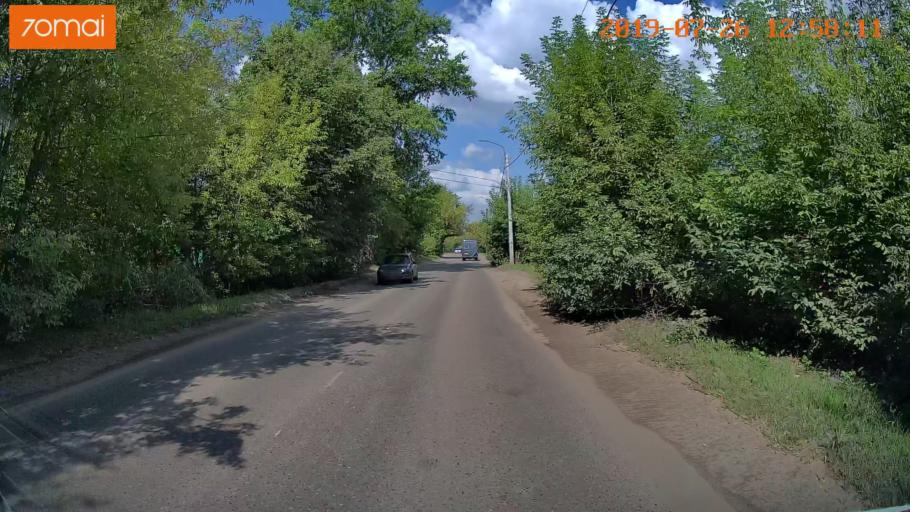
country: RU
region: Ivanovo
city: Bogorodskoye
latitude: 57.0226
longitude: 41.0208
